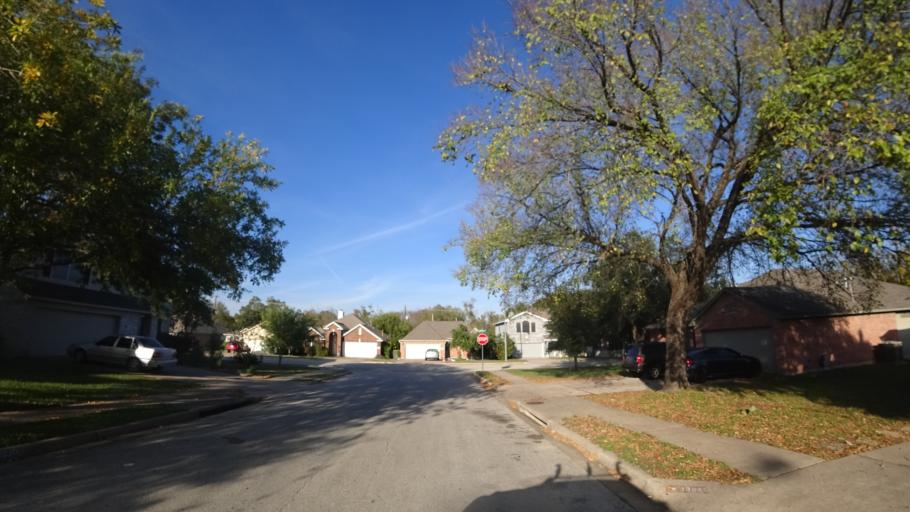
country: US
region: Texas
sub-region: Travis County
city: Pflugerville
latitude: 30.4191
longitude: -97.6524
